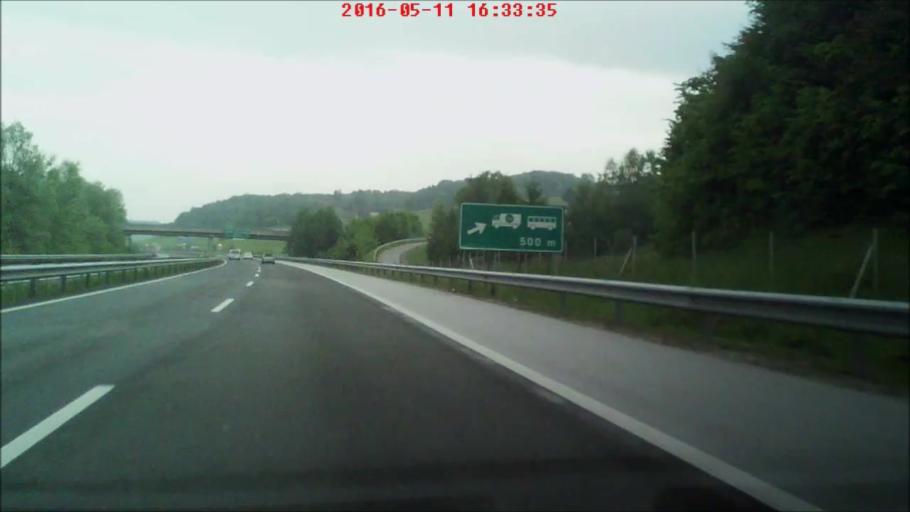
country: SI
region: Pesnica
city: Pesnica pri Mariboru
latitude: 46.6253
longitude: 15.6577
